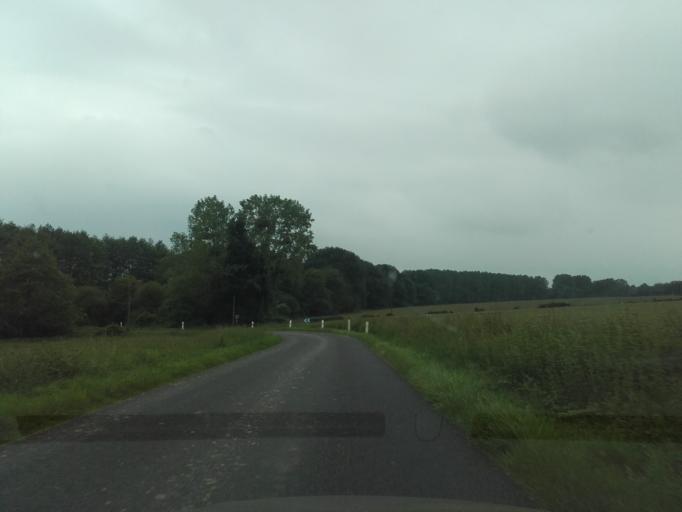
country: FR
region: Pays de la Loire
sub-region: Departement de la Sarthe
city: Ruille-sur-Loir
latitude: 47.6848
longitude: 0.6781
